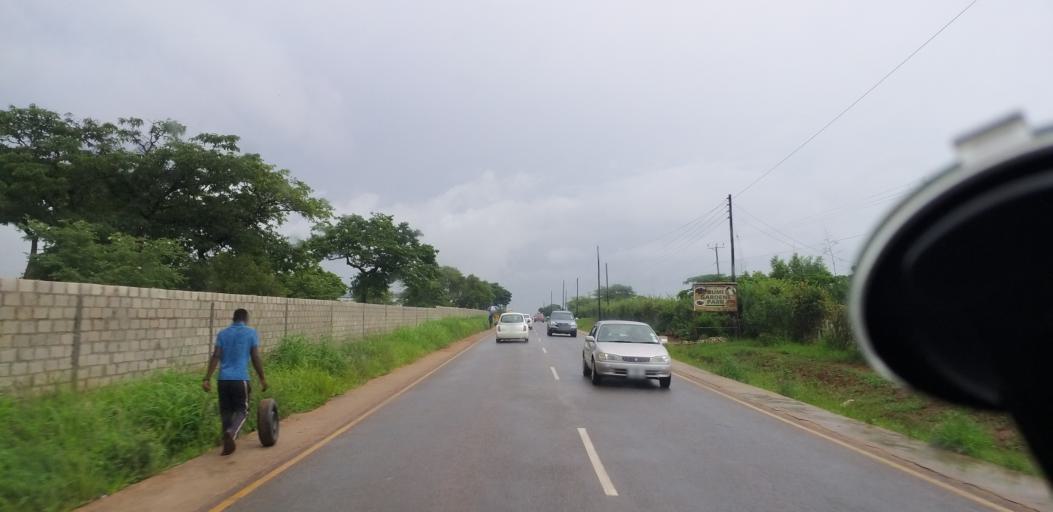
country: ZM
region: Lusaka
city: Lusaka
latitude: -15.5122
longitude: 28.3114
